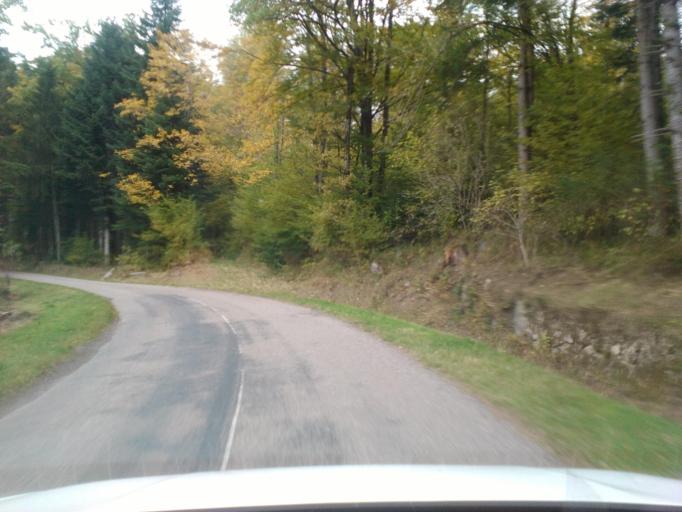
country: FR
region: Lorraine
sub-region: Departement des Vosges
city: Sainte-Marguerite
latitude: 48.3276
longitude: 7.0236
